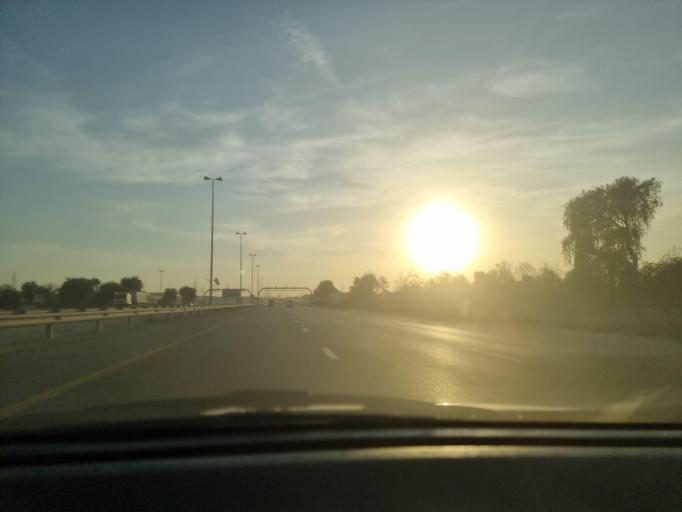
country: AE
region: Abu Dhabi
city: Abu Dhabi
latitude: 24.3055
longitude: 54.6701
